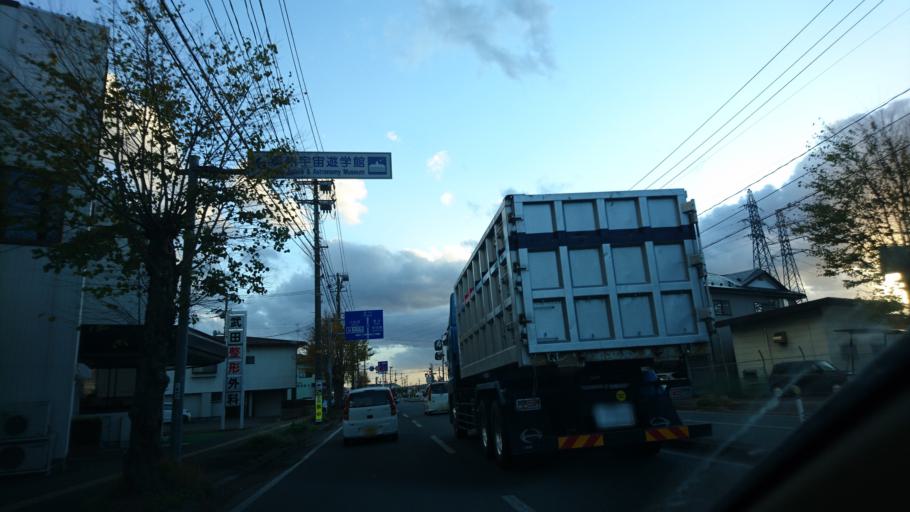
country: JP
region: Iwate
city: Mizusawa
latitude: 39.1429
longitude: 141.1289
